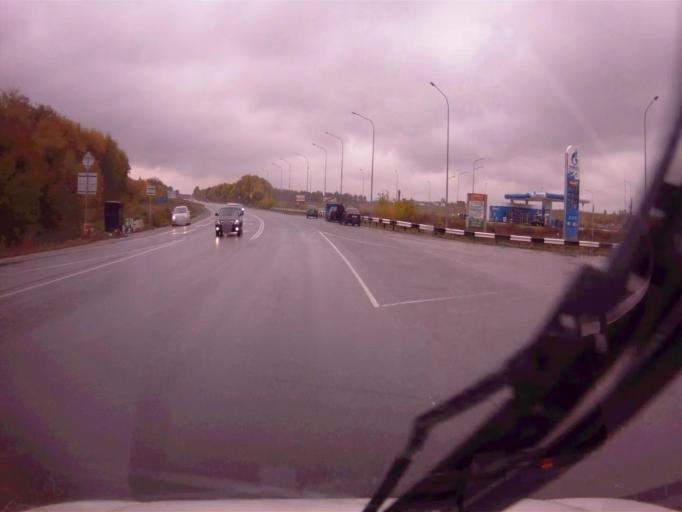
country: RU
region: Chelyabinsk
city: Roshchino
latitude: 55.3694
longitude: 61.1832
